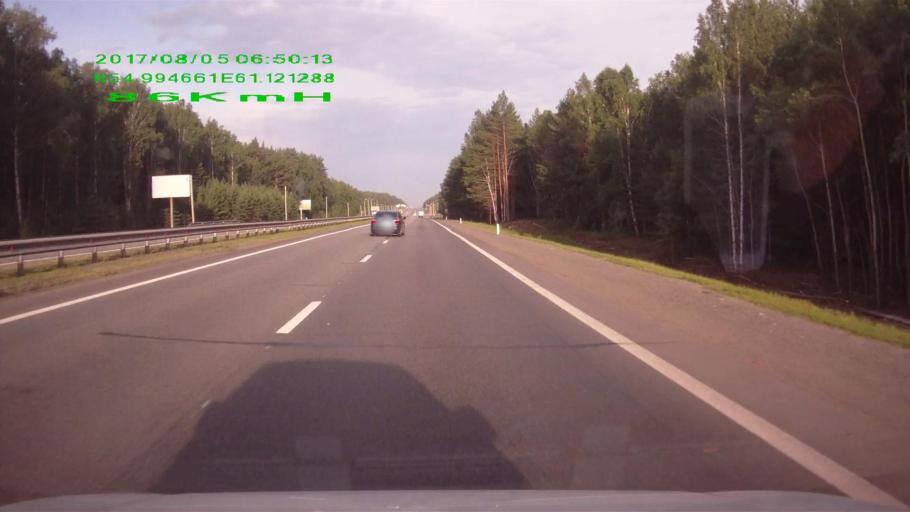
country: RU
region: Chelyabinsk
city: Poletayevo
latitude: 54.9946
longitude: 61.1209
